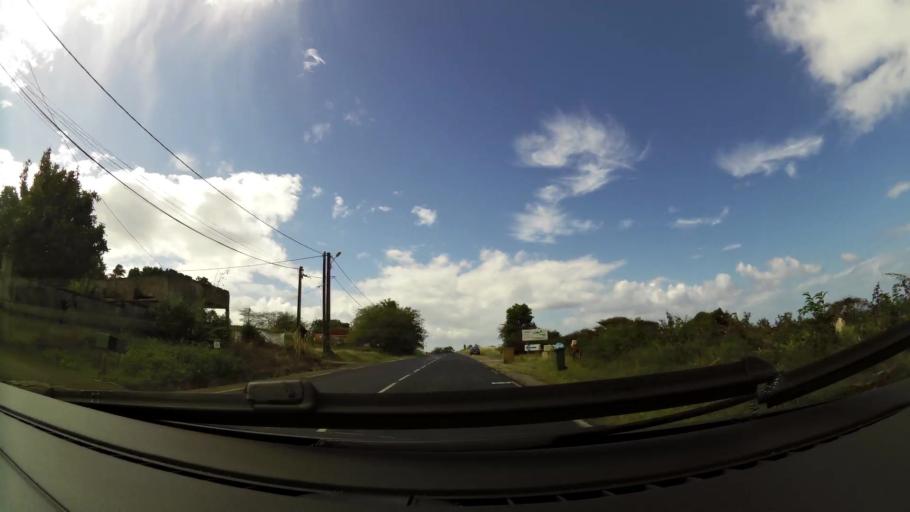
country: GP
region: Guadeloupe
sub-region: Guadeloupe
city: Sainte-Rose
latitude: 16.3539
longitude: -61.7415
